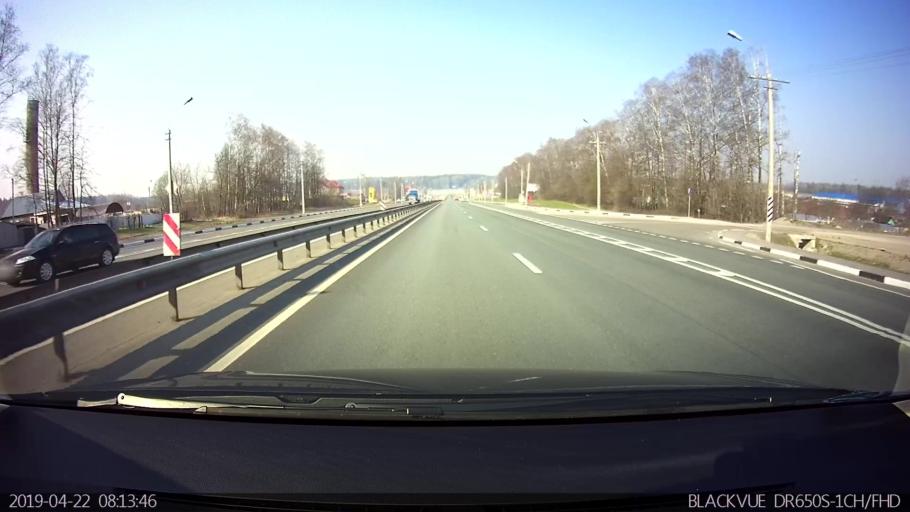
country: RU
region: Smolensk
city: Yartsevo
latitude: 55.0815
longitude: 32.7594
